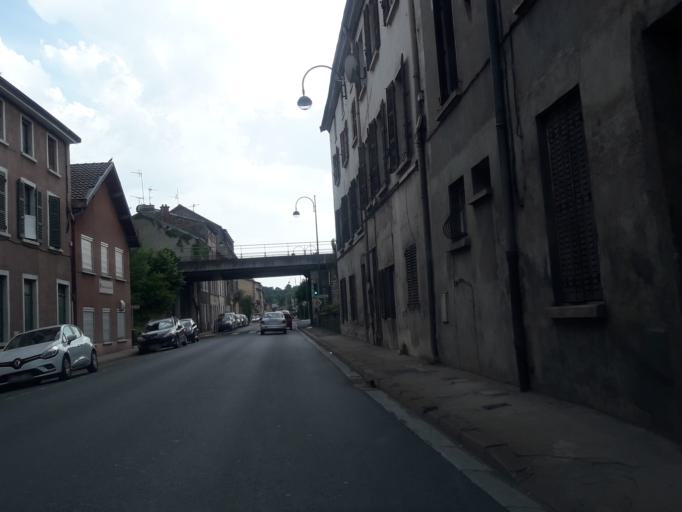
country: FR
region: Rhone-Alpes
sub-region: Departement du Rhone
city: Saint-Germain-Nuelles
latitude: 45.8335
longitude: 4.6142
